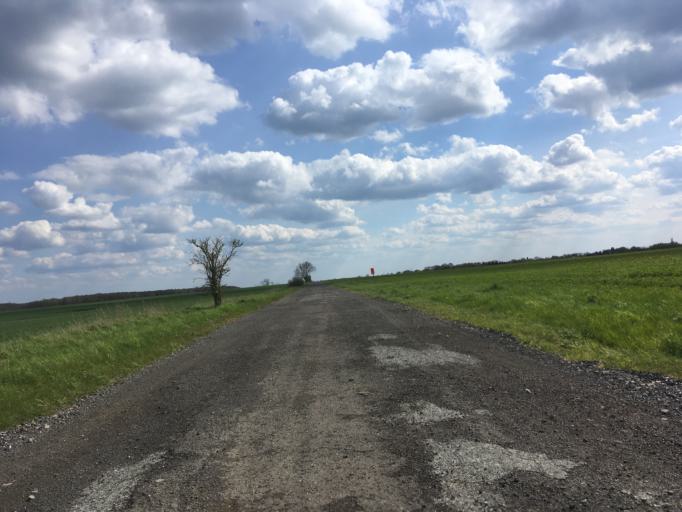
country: DE
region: Brandenburg
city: Werneuchen
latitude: 52.6091
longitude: 13.6998
